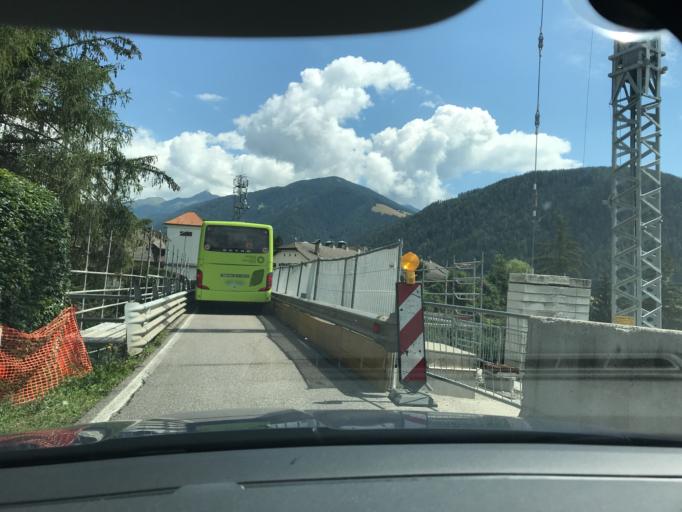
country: IT
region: Trentino-Alto Adige
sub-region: Bolzano
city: Valdaora di Mezzo
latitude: 46.7712
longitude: 12.0324
